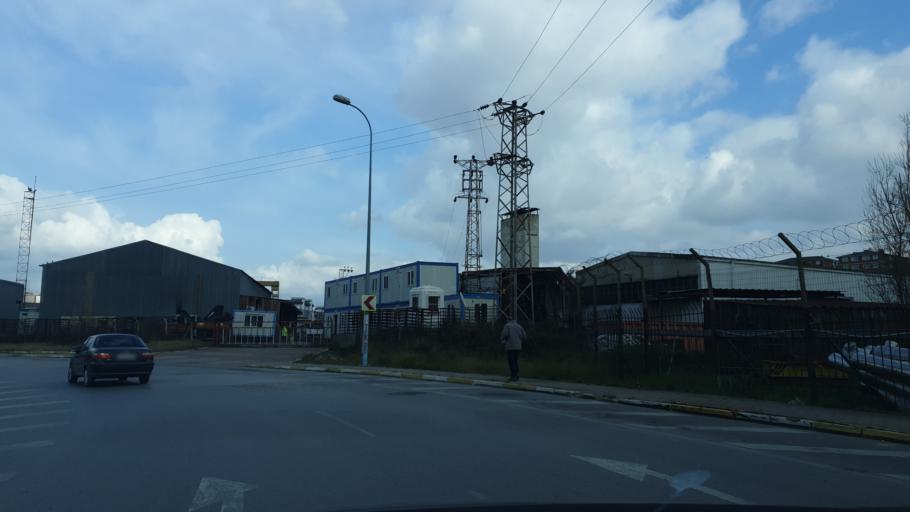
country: TR
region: Istanbul
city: Pendik
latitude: 40.8653
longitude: 29.2789
